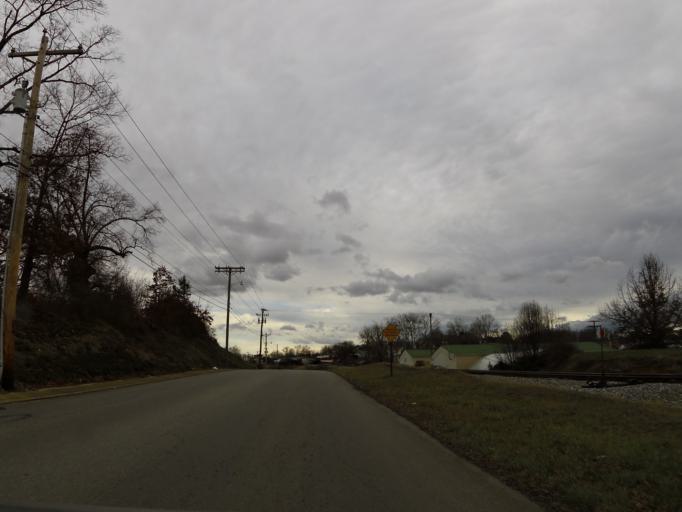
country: US
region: Tennessee
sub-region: Greene County
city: Greeneville
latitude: 36.1573
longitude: -82.8442
